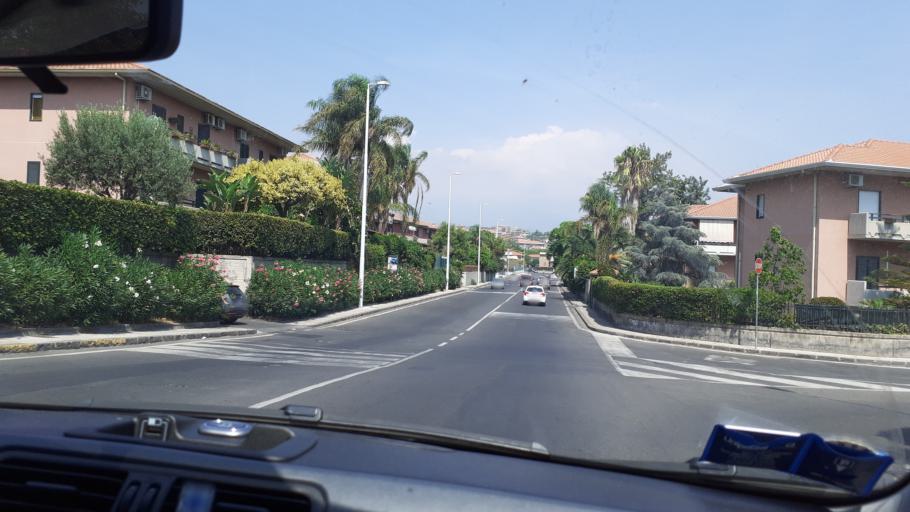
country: IT
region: Sicily
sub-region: Catania
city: Catania
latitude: 37.5136
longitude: 15.0563
